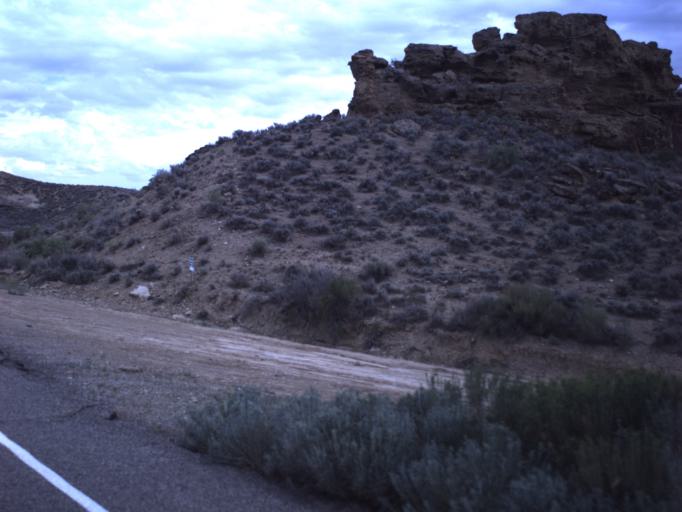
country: US
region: Colorado
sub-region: Rio Blanco County
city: Rangely
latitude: 39.9754
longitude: -109.1736
